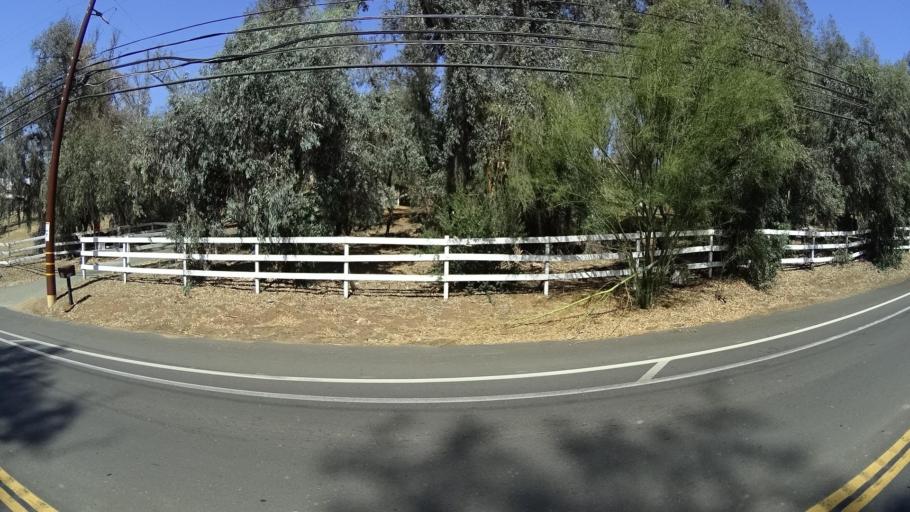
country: US
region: California
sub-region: San Diego County
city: Granite Hills
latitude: 32.7874
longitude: -116.9158
